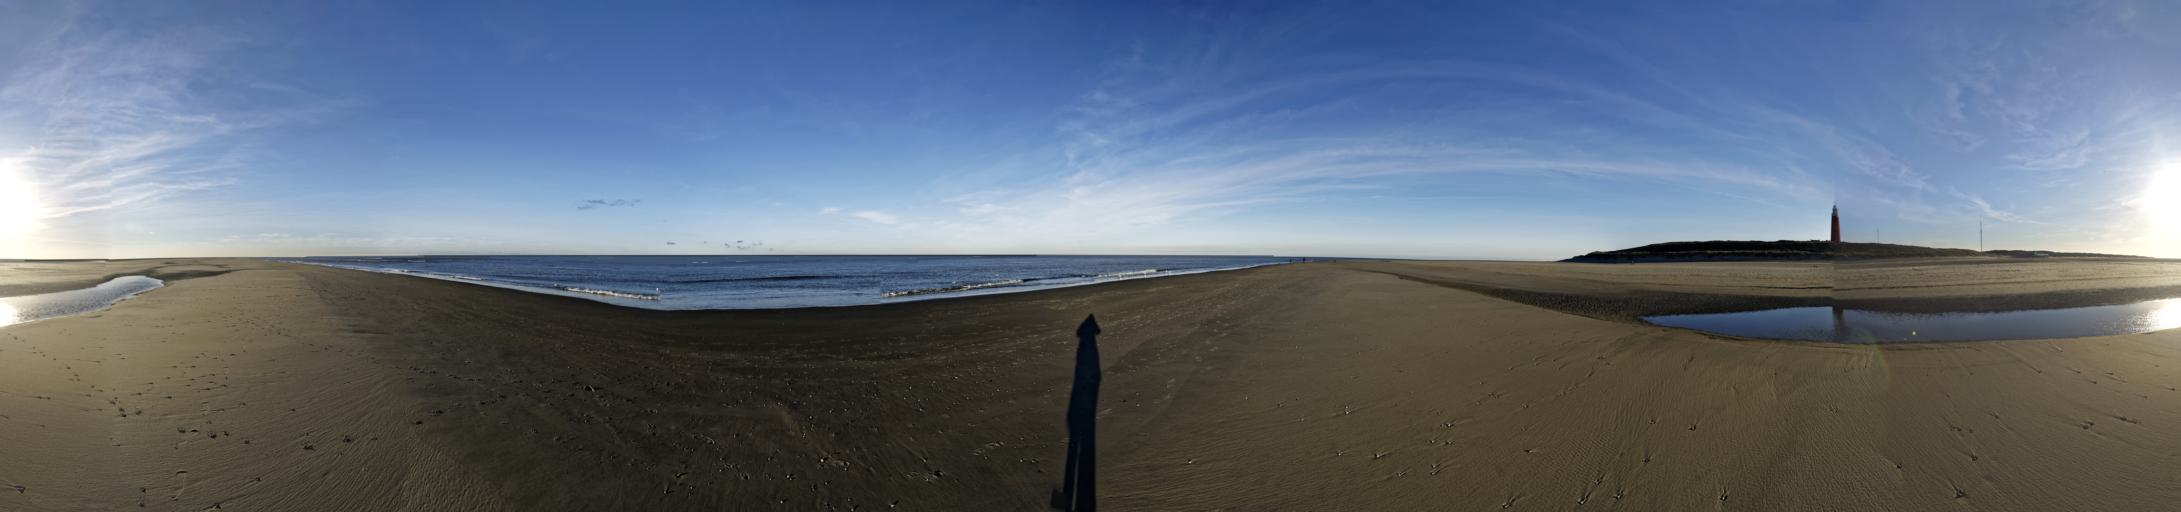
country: NL
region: North Holland
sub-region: Gemeente Texel
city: Den Burg
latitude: 53.1847
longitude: 4.8549
